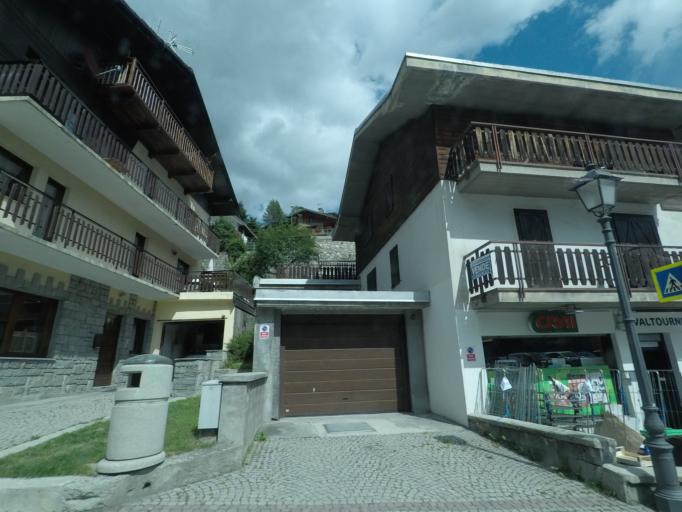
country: IT
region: Aosta Valley
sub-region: Valle d'Aosta
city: Valtournenche
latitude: 45.8783
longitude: 7.6233
